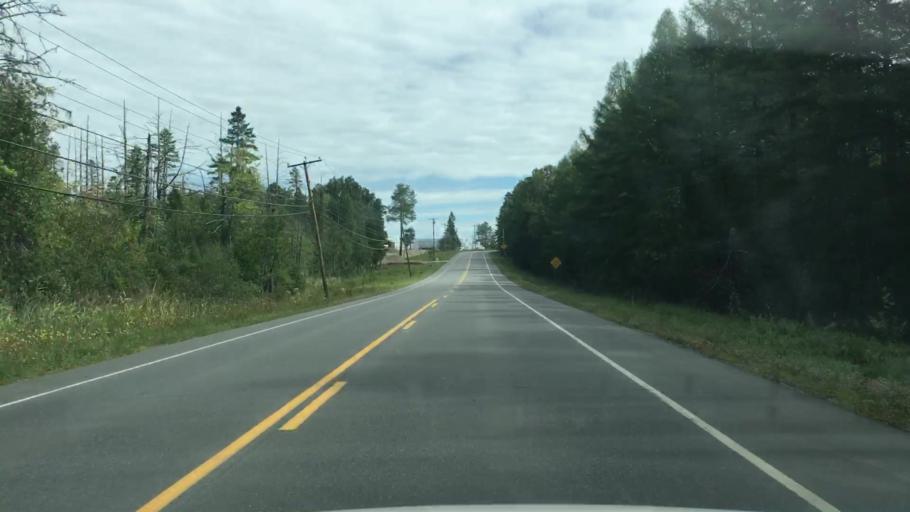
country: US
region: Maine
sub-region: Piscataquis County
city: Dover-Foxcroft
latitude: 45.1998
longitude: -69.2009
